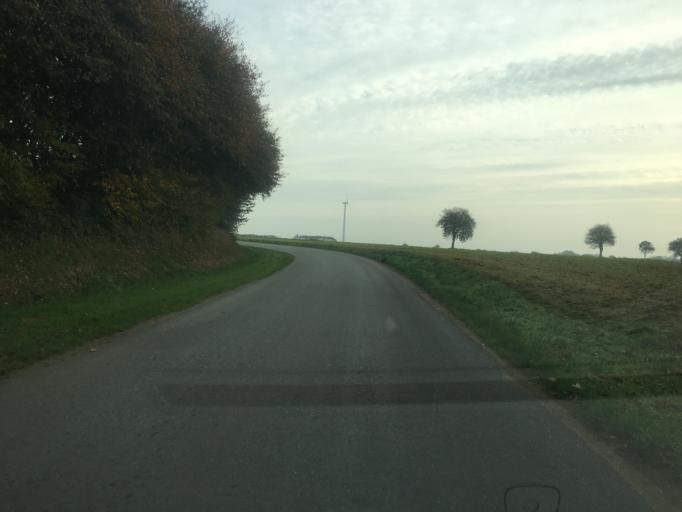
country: DK
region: South Denmark
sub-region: Tonder Kommune
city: Toftlund
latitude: 55.1040
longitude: 9.0871
